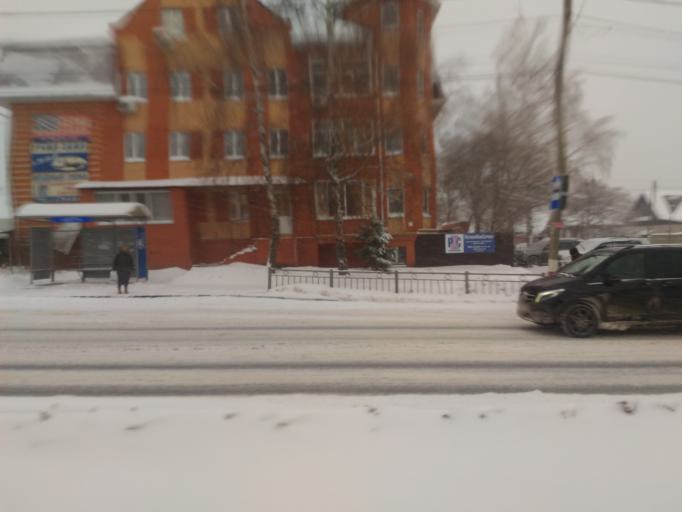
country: RU
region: Ulyanovsk
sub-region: Ulyanovskiy Rayon
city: Ulyanovsk
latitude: 54.3502
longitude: 48.3825
